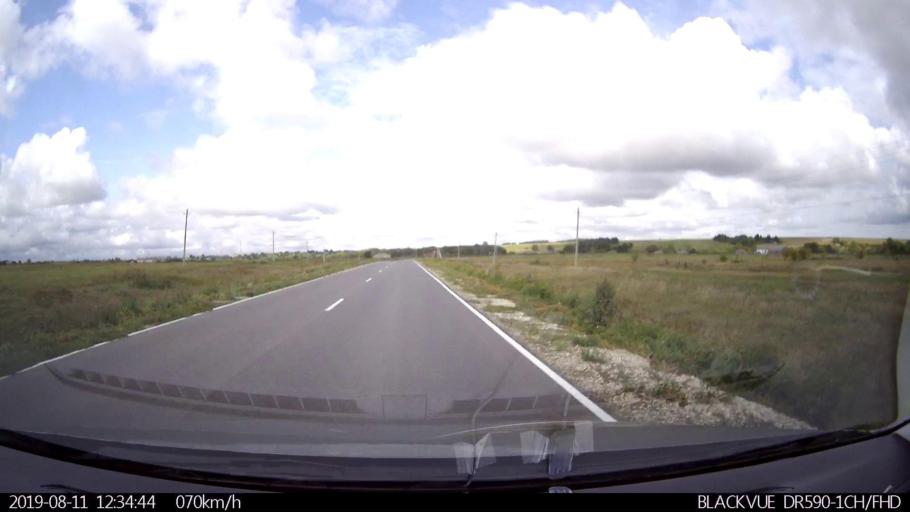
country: RU
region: Ulyanovsk
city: Ignatovka
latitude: 53.8191
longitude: 47.8388
